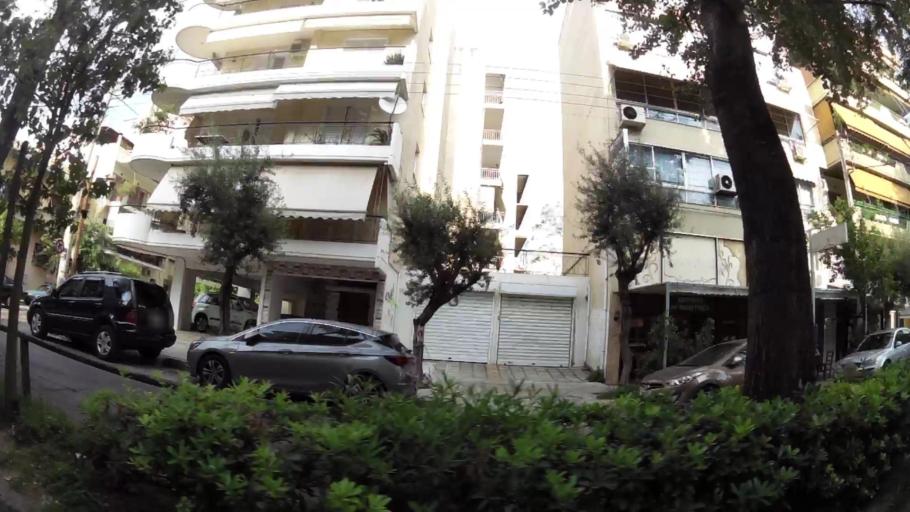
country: GR
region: Attica
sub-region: Nomarchia Athinas
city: Kallithea
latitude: 37.9487
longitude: 23.7014
